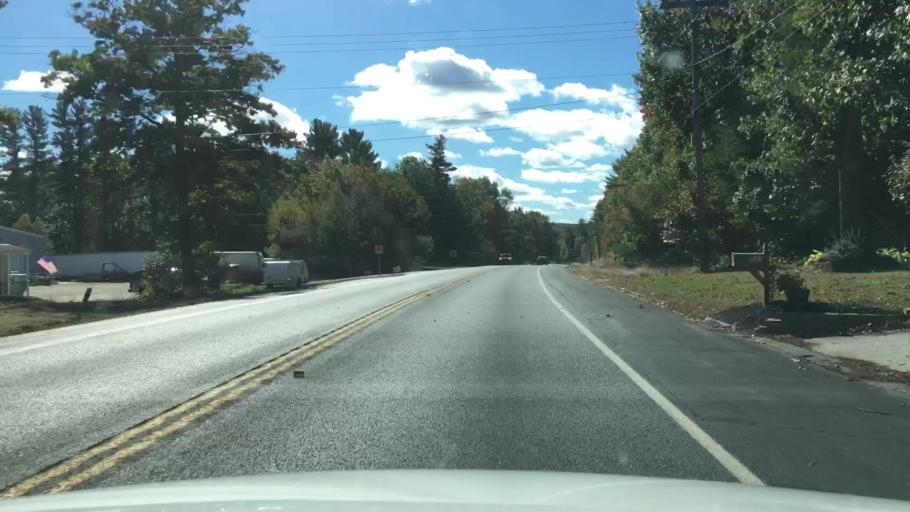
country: US
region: Maine
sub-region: York County
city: Alfred
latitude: 43.4493
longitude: -70.7260
